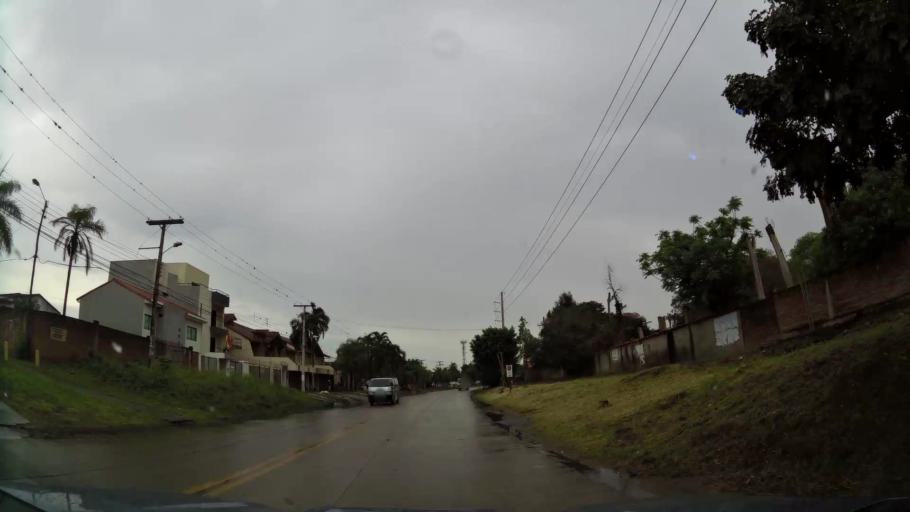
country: BO
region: Santa Cruz
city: Santa Cruz de la Sierra
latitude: -17.8033
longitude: -63.1598
